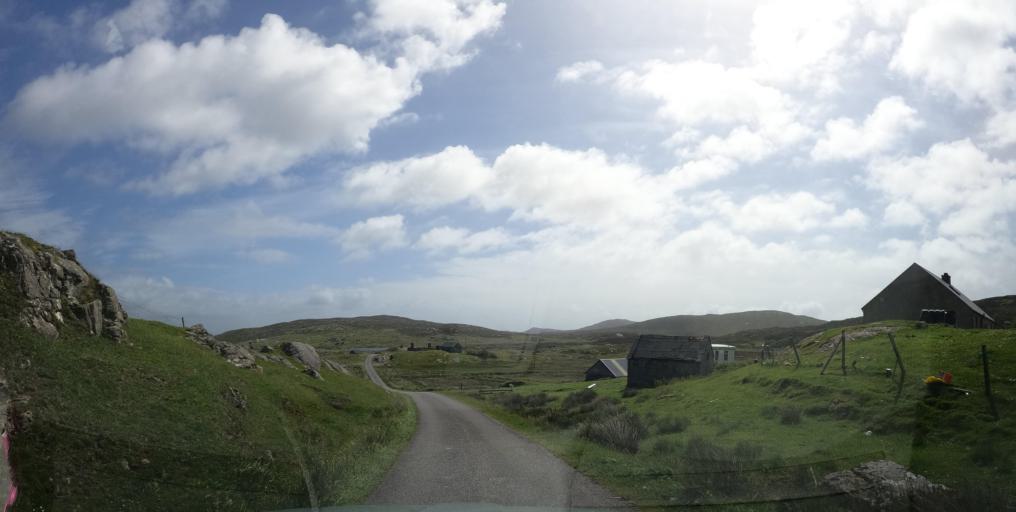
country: GB
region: Scotland
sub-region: Eilean Siar
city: Isle of South Uist
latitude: 57.1355
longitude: -7.3190
